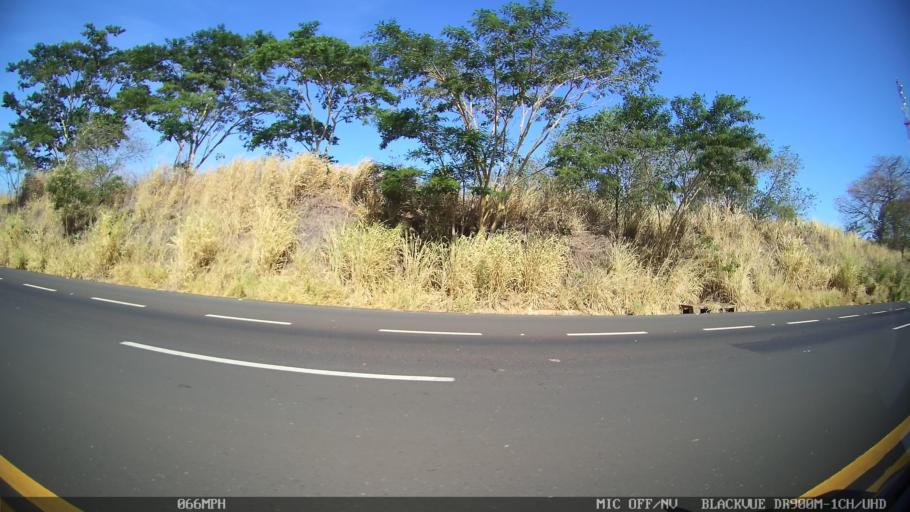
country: BR
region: Sao Paulo
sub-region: Barretos
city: Barretos
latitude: -20.6104
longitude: -48.7515
